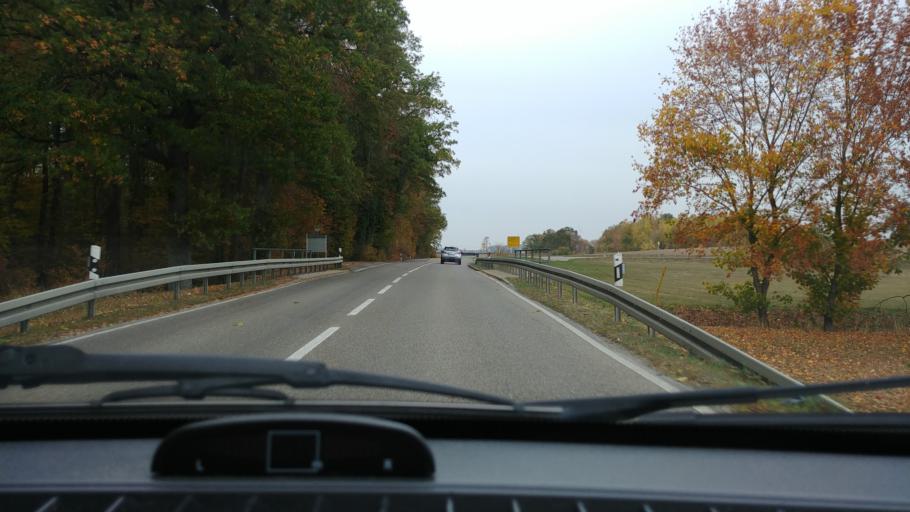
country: DE
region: Baden-Wuerttemberg
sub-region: Regierungsbezirk Stuttgart
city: Wallhausen
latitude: 49.2271
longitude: 10.0509
